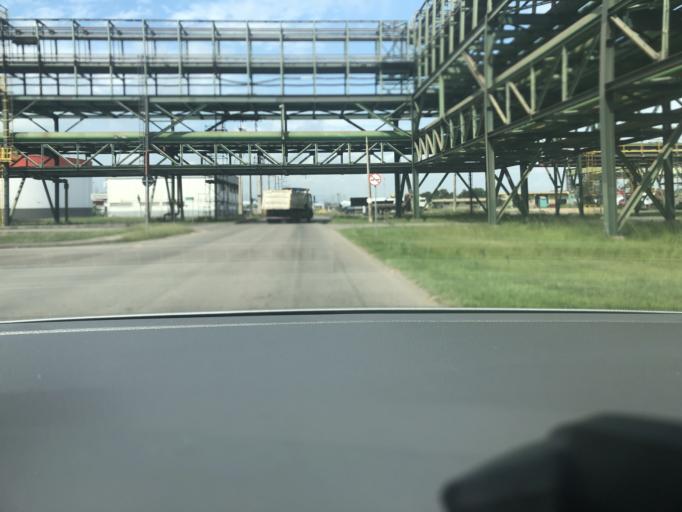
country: BR
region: Rio de Janeiro
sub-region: Itaguai
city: Itaguai
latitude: -22.9044
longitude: -43.7375
